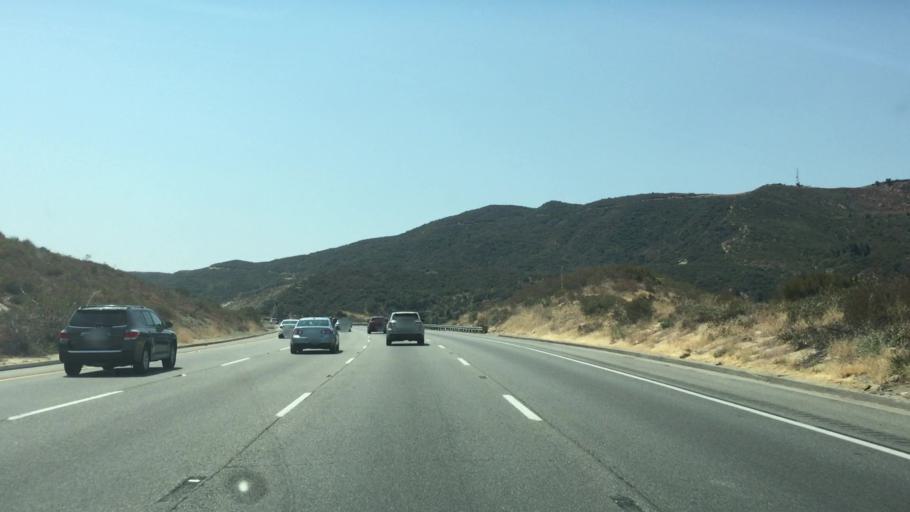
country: US
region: California
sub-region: Los Angeles County
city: Castaic
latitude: 34.5967
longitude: -118.7121
